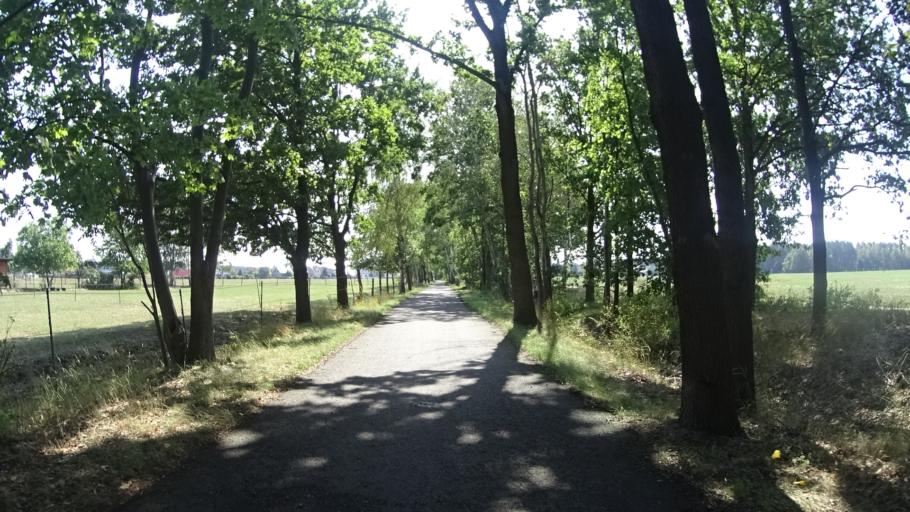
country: DE
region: Brandenburg
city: Cottbus
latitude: 51.7956
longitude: 14.2980
